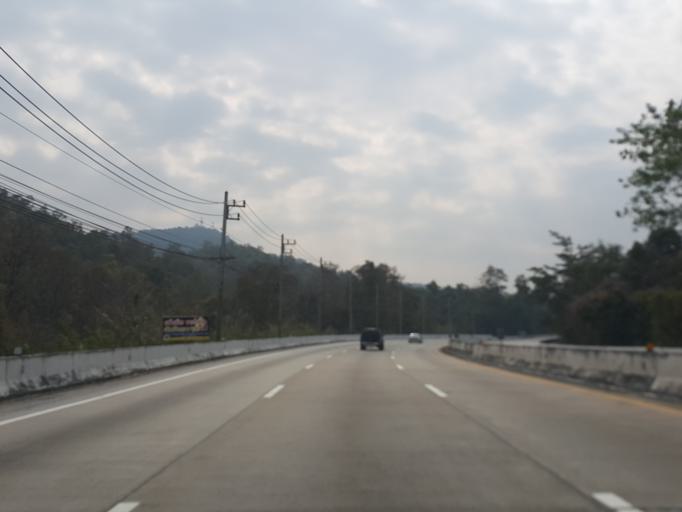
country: TH
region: Lamphun
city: Mae Tha
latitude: 18.4461
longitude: 99.2047
